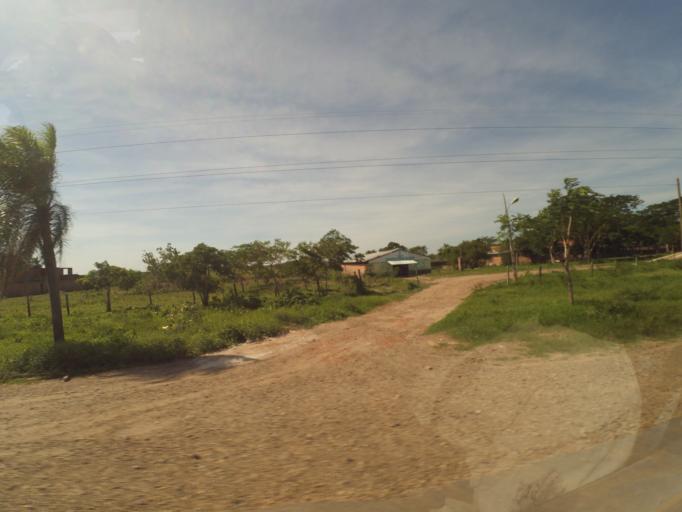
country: BO
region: Santa Cruz
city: San Julian
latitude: -17.7420
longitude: -62.9481
